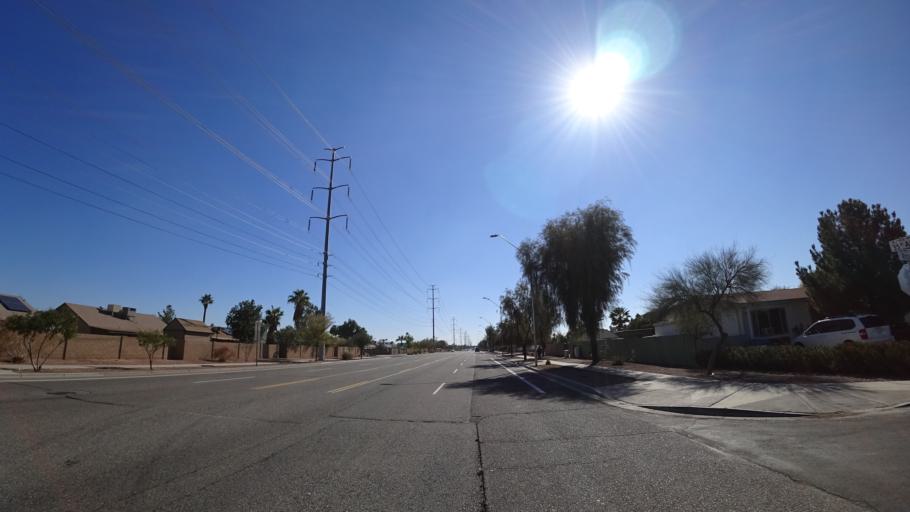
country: US
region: Arizona
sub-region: Maricopa County
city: Peoria
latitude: 33.6781
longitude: -112.1348
